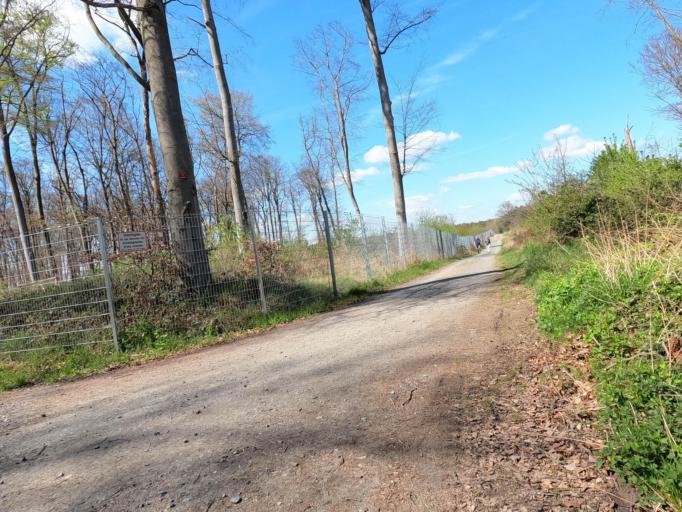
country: DE
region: Hesse
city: Raunheim
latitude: 50.0123
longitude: 8.4875
